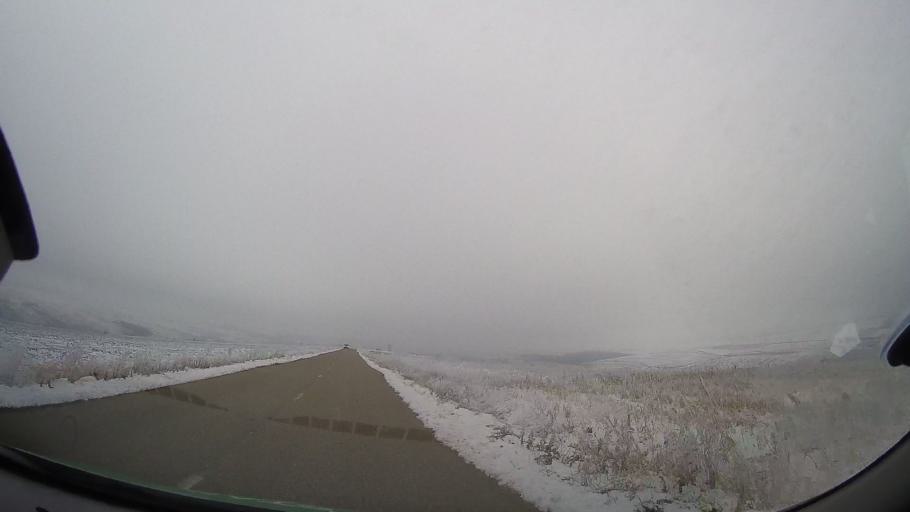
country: RO
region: Vaslui
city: Coroiesti
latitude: 46.2155
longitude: 27.4806
